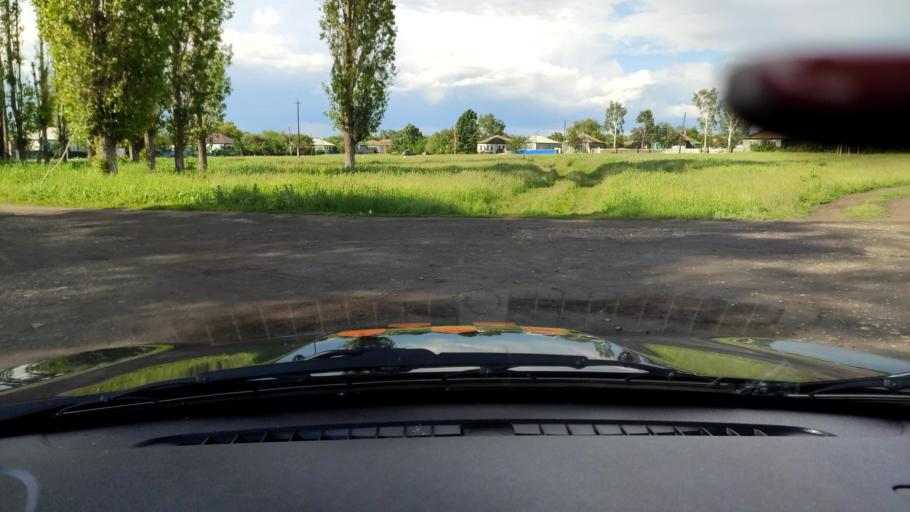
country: RU
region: Voronezj
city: Uryv-Pokrovka
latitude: 51.1163
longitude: 39.1834
